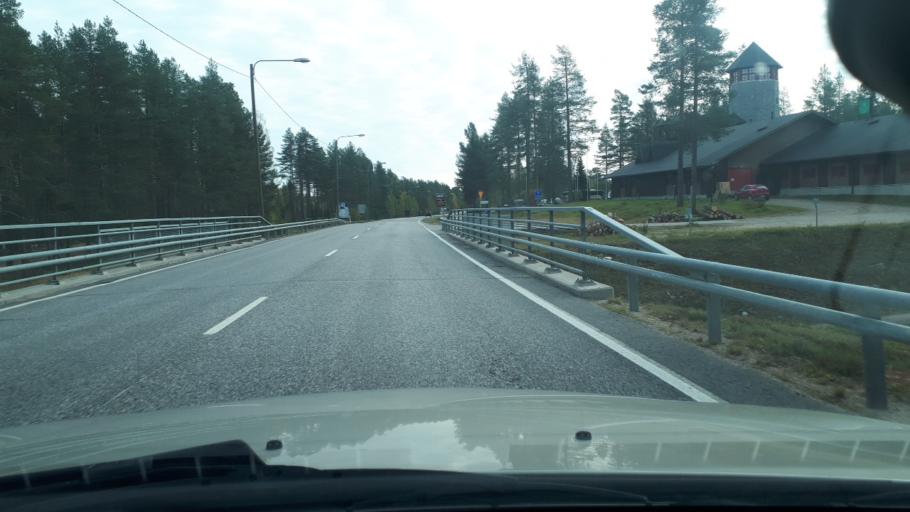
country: FI
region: Lapland
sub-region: Rovaniemi
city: Ranua
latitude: 65.9447
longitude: 26.4651
